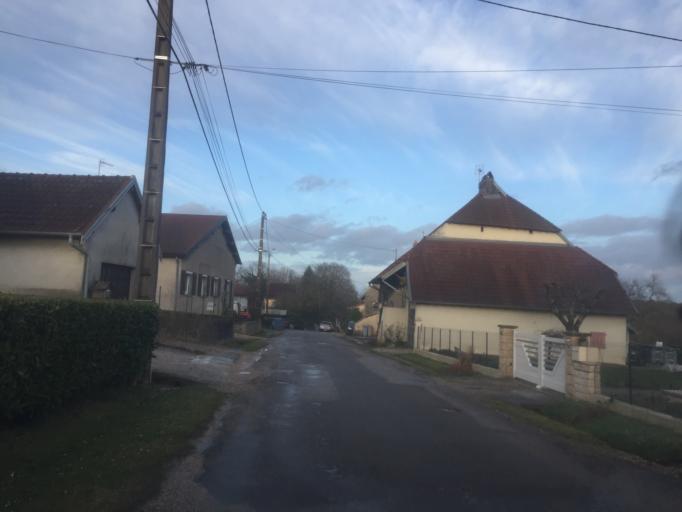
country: FR
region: Franche-Comte
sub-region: Departement du Jura
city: Dampierre
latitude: 47.1253
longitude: 5.7130
